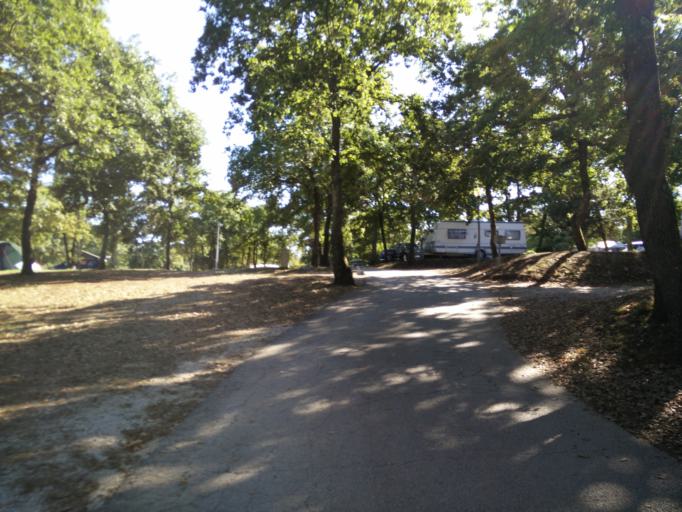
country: HR
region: Istarska
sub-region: Grad Porec
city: Porec
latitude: 45.1883
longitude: 13.5924
